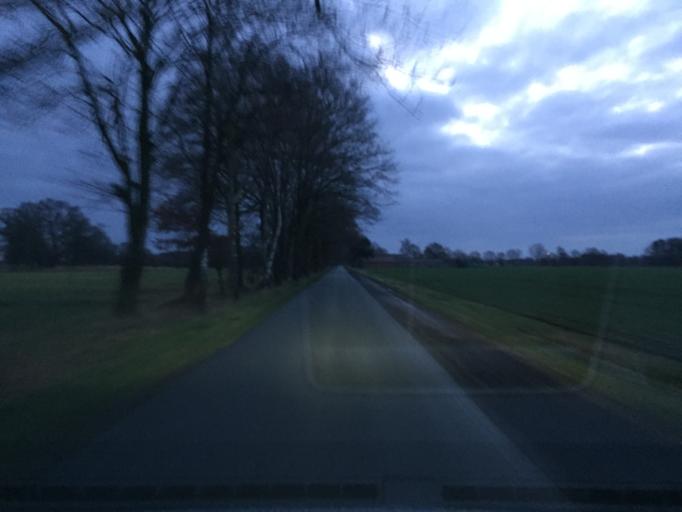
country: DE
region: Lower Saxony
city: Kirchdorf
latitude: 52.6323
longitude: 8.8591
